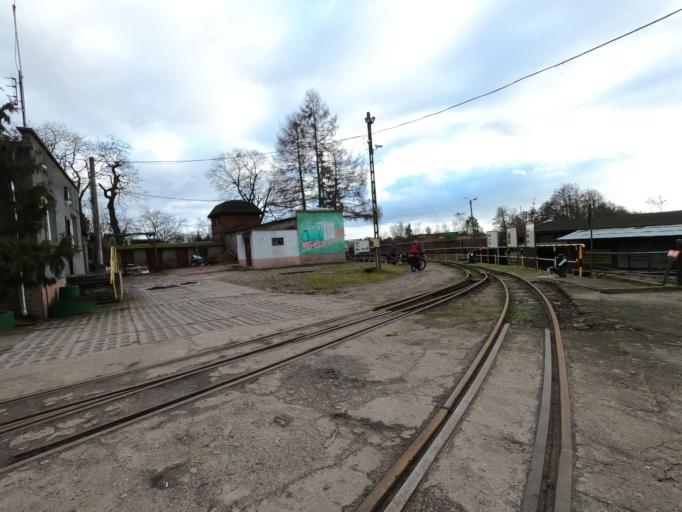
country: PL
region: Greater Poland Voivodeship
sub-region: Powiat pilski
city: Bialosliwie
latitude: 53.0969
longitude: 17.1171
